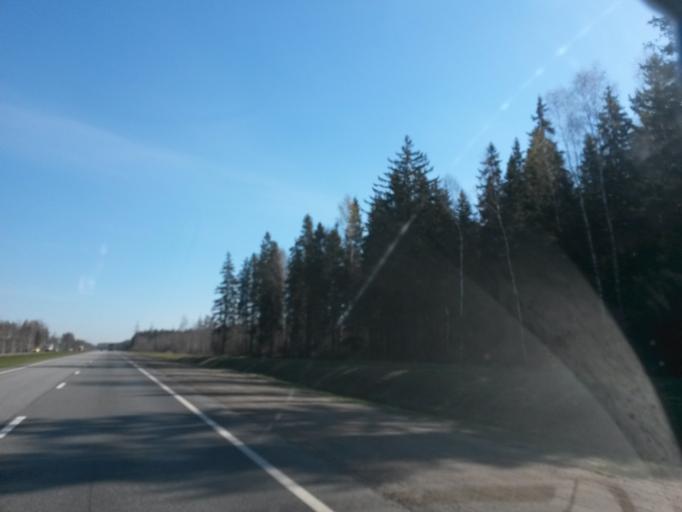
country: RU
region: Jaroslavl
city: Krasnyye Tkachi
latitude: 57.4740
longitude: 39.7623
